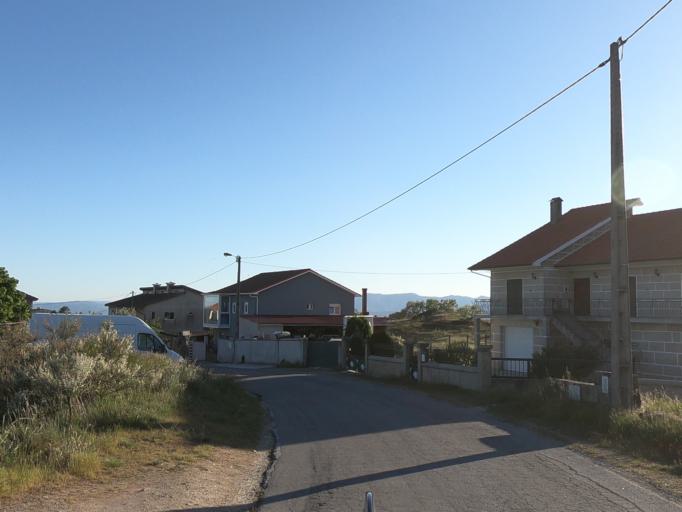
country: PT
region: Vila Real
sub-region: Vila Real
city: Vila Real
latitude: 41.3564
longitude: -7.6619
